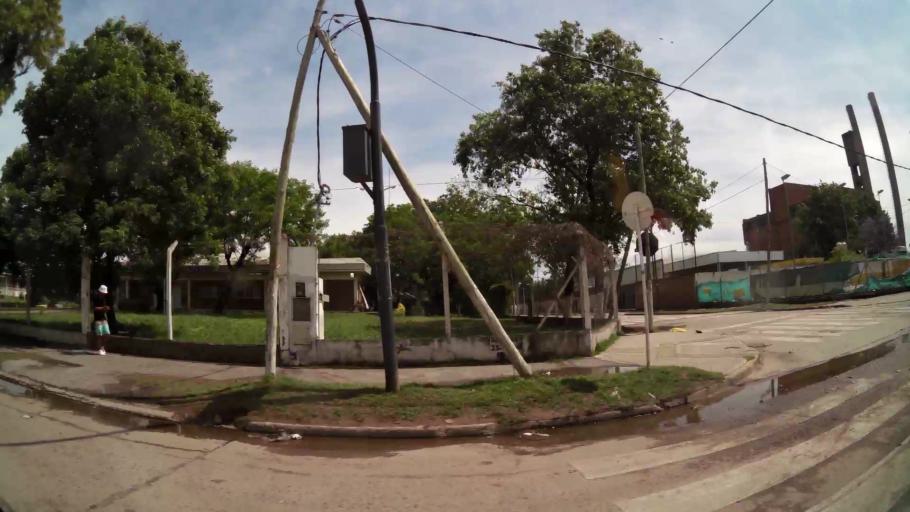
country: AR
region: Buenos Aires F.D.
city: Villa Lugano
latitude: -34.6548
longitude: -58.4395
